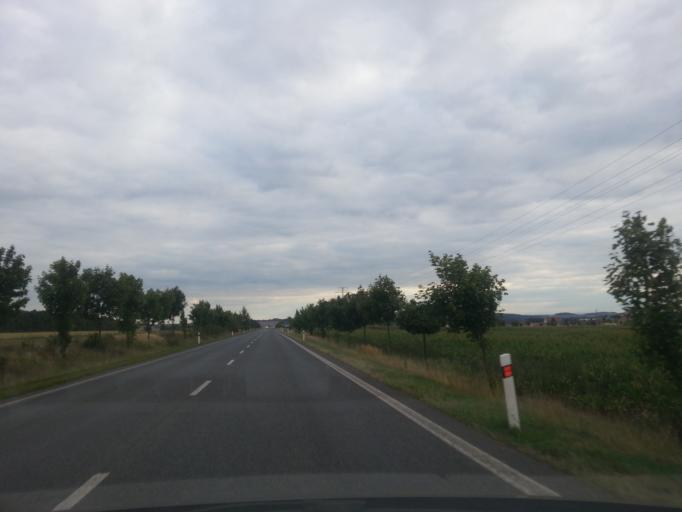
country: CZ
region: Central Bohemia
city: Unhost'
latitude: 50.0941
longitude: 14.1397
